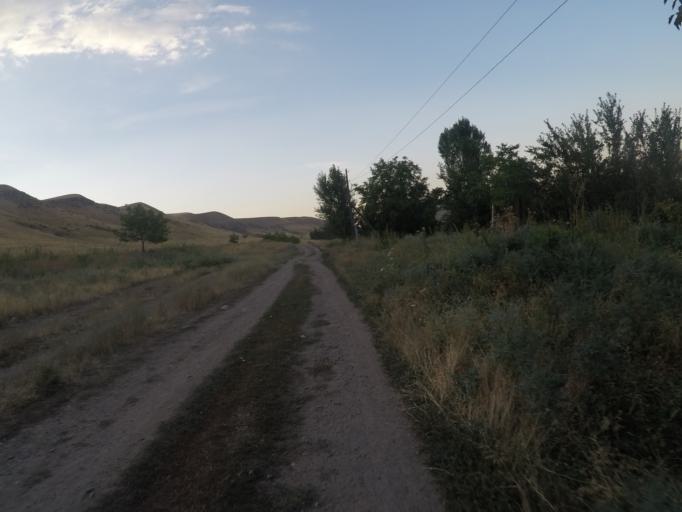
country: KG
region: Chuy
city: Bishkek
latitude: 42.7687
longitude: 74.6387
